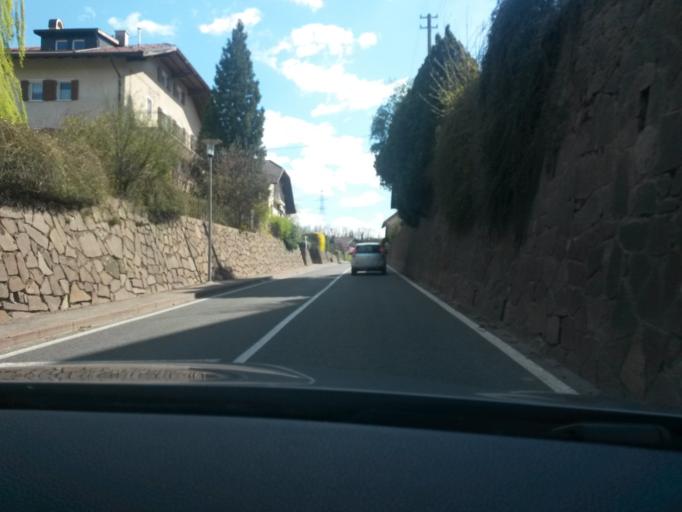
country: IT
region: Trentino-Alto Adige
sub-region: Bolzano
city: San Michele
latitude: 46.4511
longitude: 11.2715
